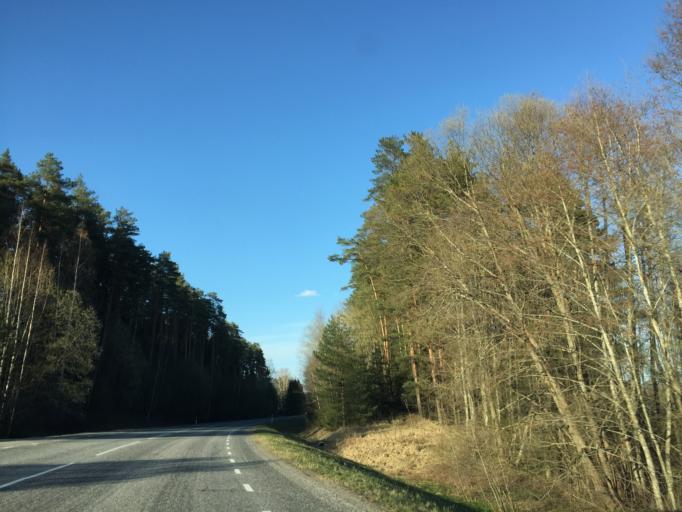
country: EE
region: Valgamaa
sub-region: Torva linn
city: Torva
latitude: 58.1050
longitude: 26.1167
